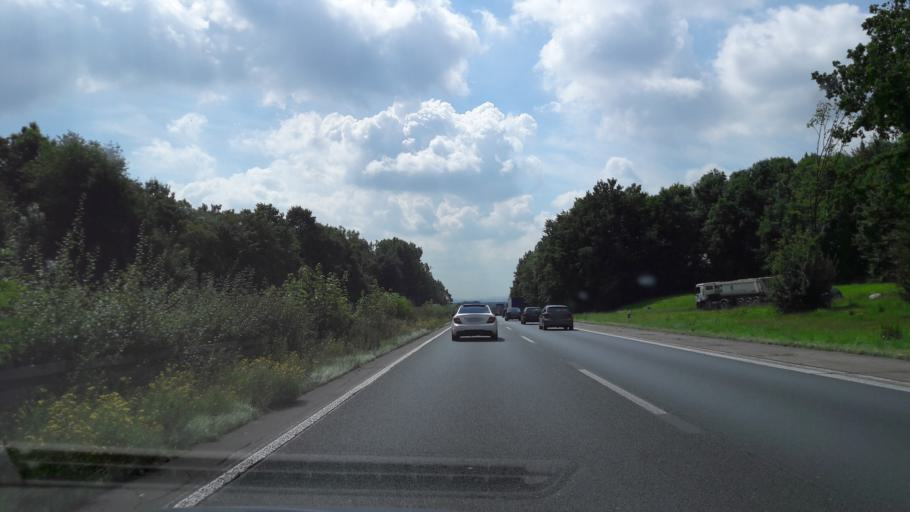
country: DE
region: North Rhine-Westphalia
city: Werne
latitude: 51.6735
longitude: 7.6804
